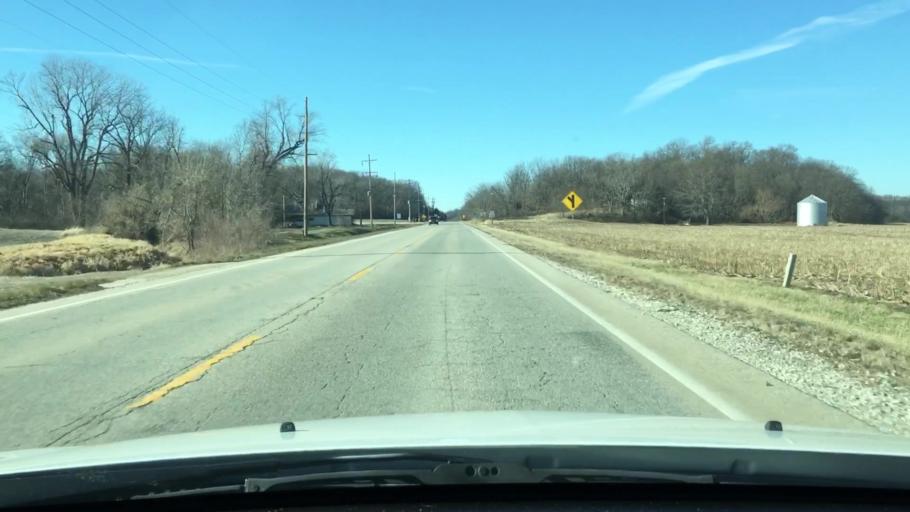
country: US
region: Illinois
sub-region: Mason County
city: Havana
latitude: 40.3047
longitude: -90.1365
